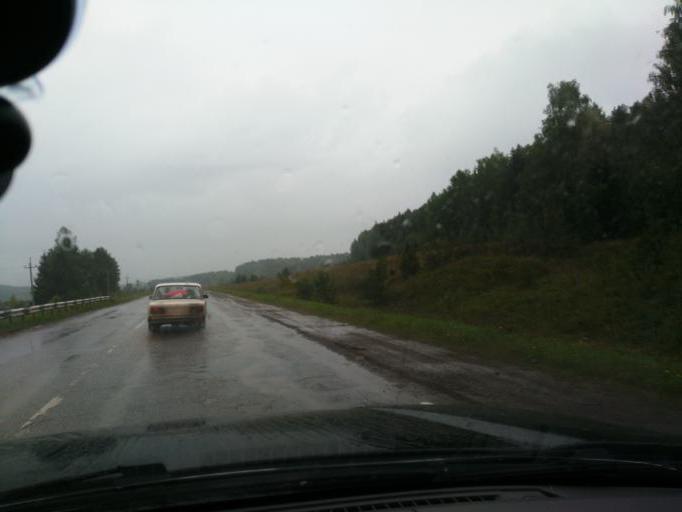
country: RU
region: Perm
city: Osa
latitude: 57.2081
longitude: 55.5891
